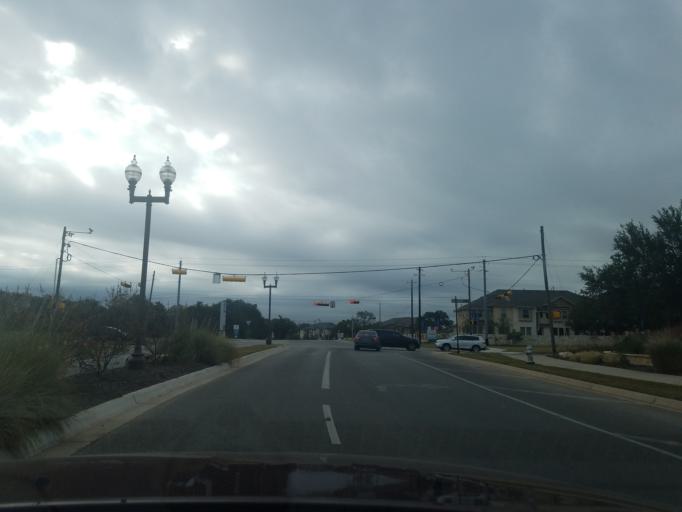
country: US
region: Texas
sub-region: Williamson County
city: Anderson Mill
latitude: 30.4824
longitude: -97.7898
